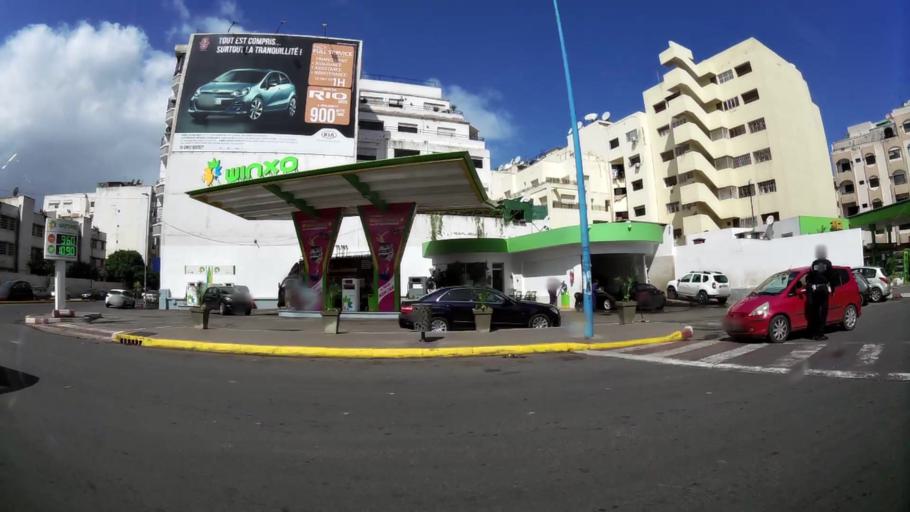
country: MA
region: Grand Casablanca
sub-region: Casablanca
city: Casablanca
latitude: 33.5739
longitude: -7.6155
